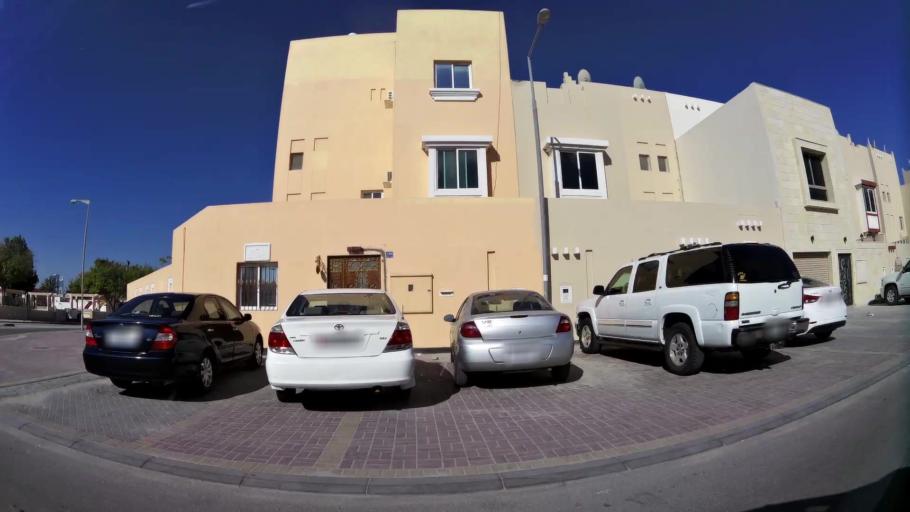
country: BH
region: Muharraq
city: Al Muharraq
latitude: 26.2567
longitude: 50.6057
